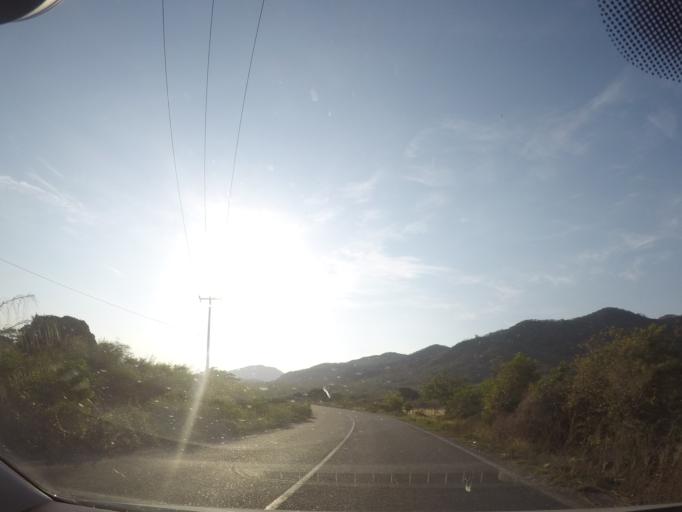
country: MX
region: Oaxaca
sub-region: Santo Domingo Tehuantepec
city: La Noria
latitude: 16.2306
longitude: -95.1788
